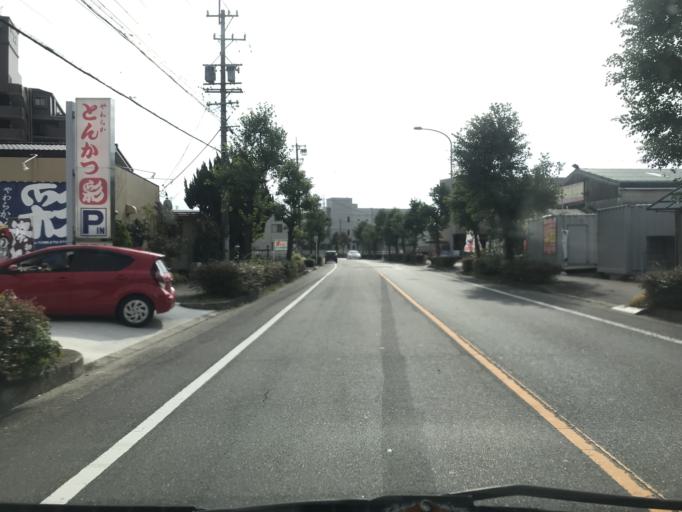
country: JP
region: Aichi
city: Nagoya-shi
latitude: 35.2028
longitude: 136.8396
